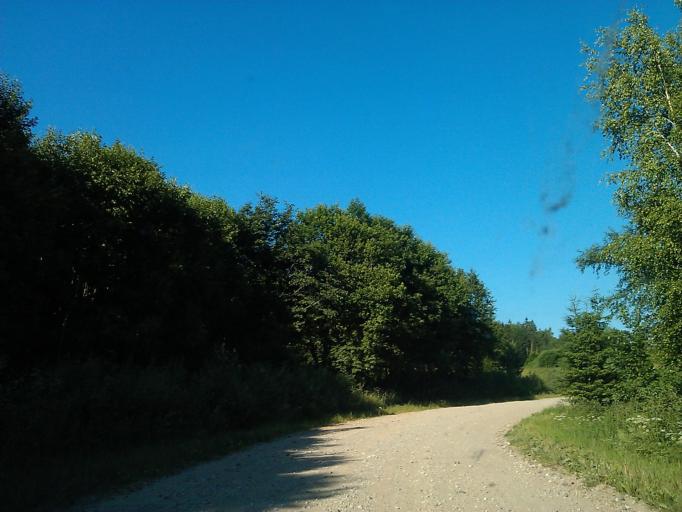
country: LV
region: Raunas
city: Rauna
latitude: 57.2560
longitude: 25.5452
